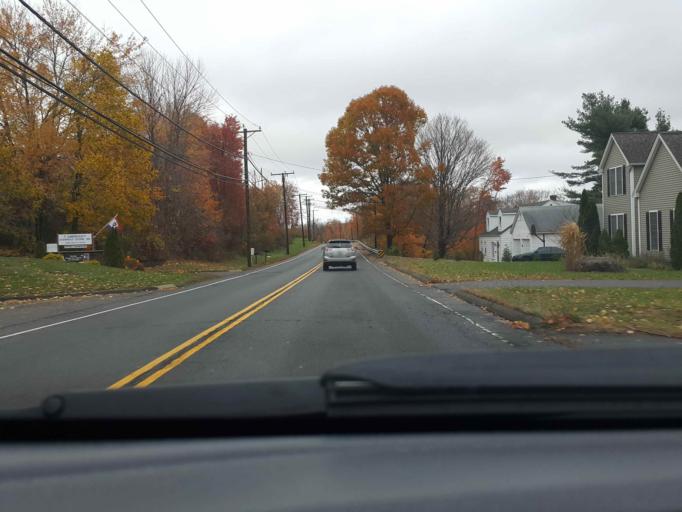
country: US
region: Connecticut
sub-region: Middlesex County
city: Durham
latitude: 41.5082
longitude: -72.6711
